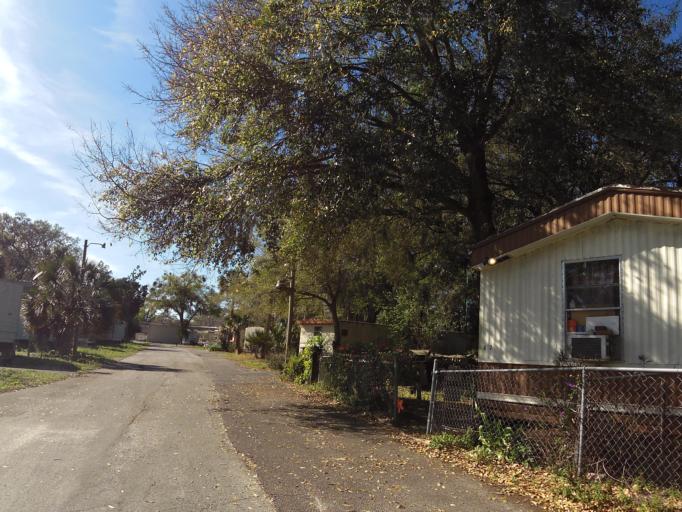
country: US
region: Florida
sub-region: Duval County
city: Jacksonville
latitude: 30.3700
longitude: -81.6499
